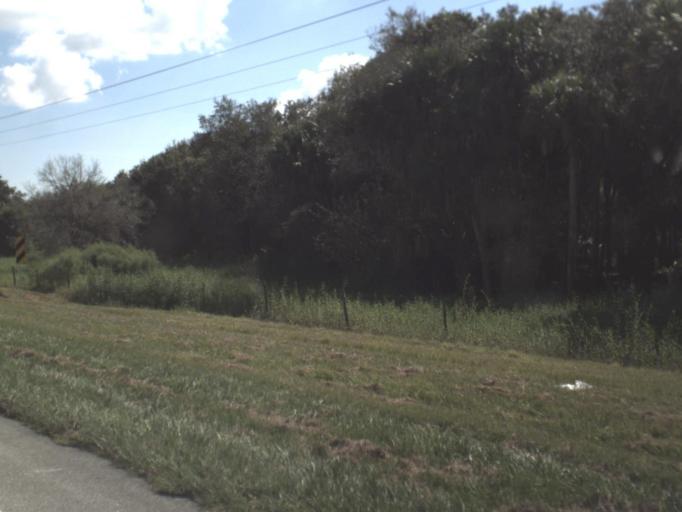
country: US
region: Florida
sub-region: Okeechobee County
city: Okeechobee
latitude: 27.3241
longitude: -80.9205
